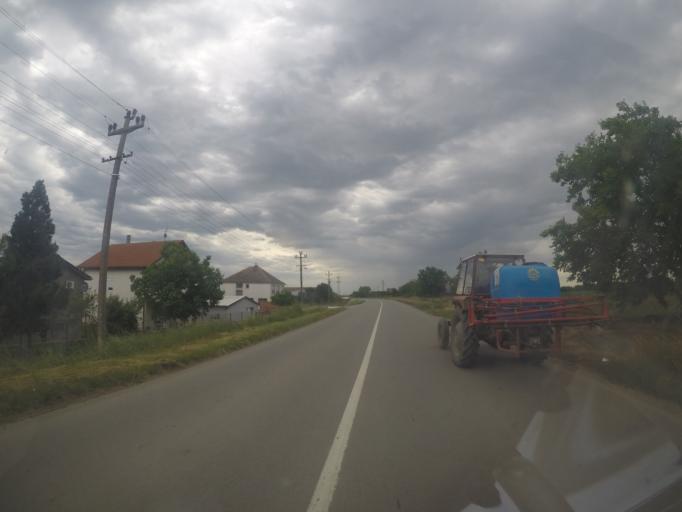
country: RS
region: Autonomna Pokrajina Vojvodina
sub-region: Juznobanatski Okrug
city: Opovo
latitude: 45.0595
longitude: 20.4344
